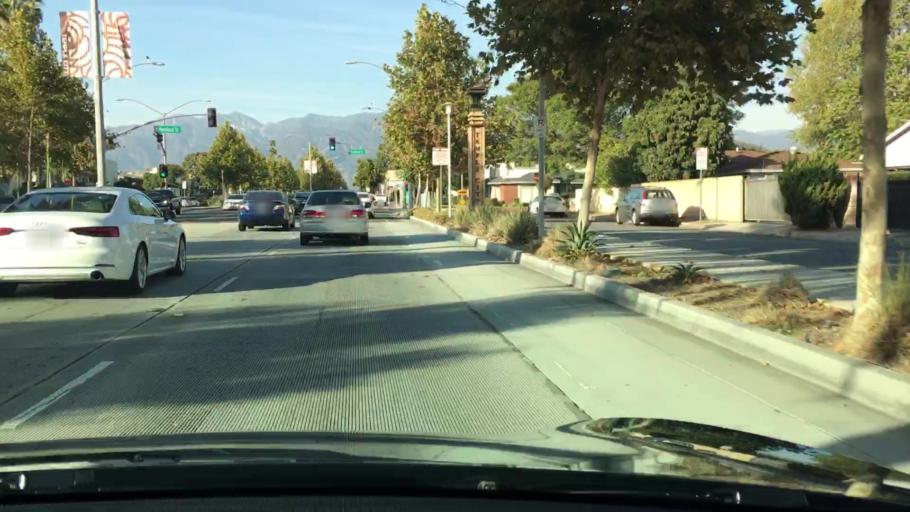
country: US
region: California
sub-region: Los Angeles County
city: Rosemead
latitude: 34.0921
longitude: -118.0733
